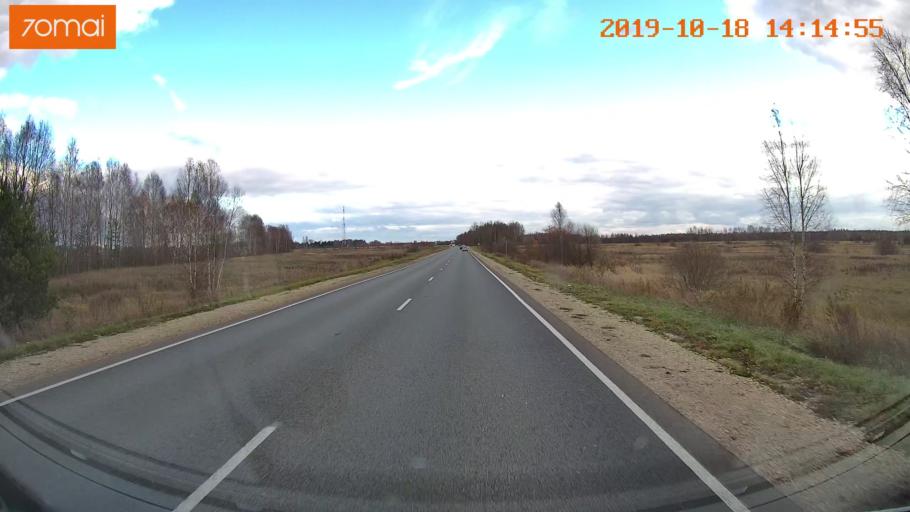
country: RU
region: Rjazan
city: Spas-Klepiki
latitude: 55.1478
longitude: 40.3056
